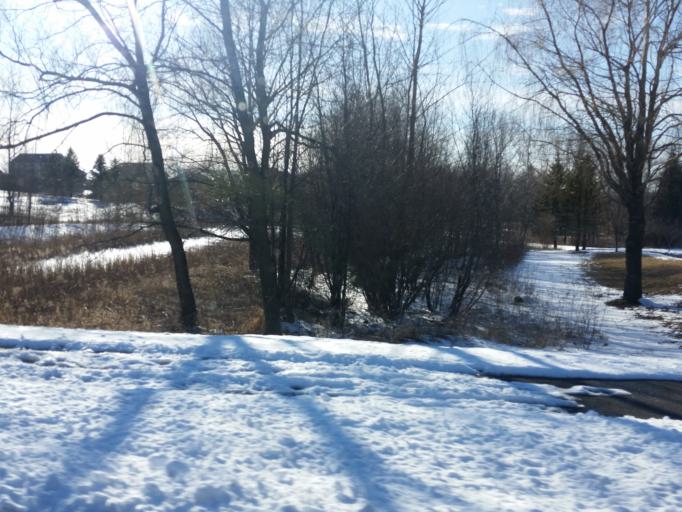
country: US
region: Minnesota
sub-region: Scott County
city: Elko New Market
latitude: 44.6334
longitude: -93.3668
